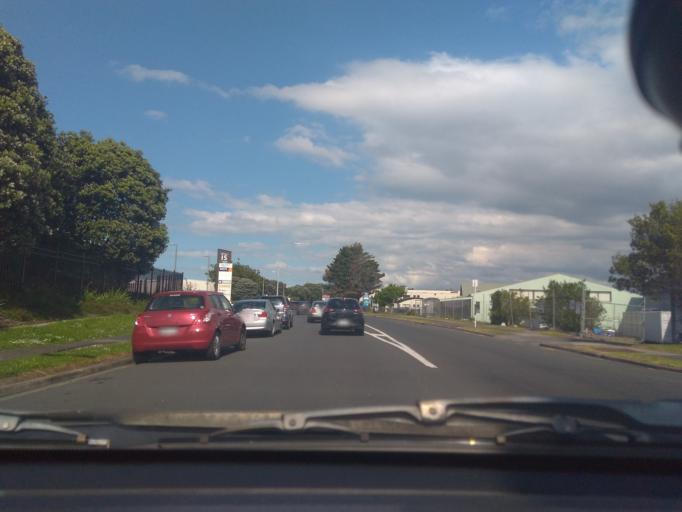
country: NZ
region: Auckland
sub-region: Auckland
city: Manukau City
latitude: -36.9470
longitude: 174.8856
